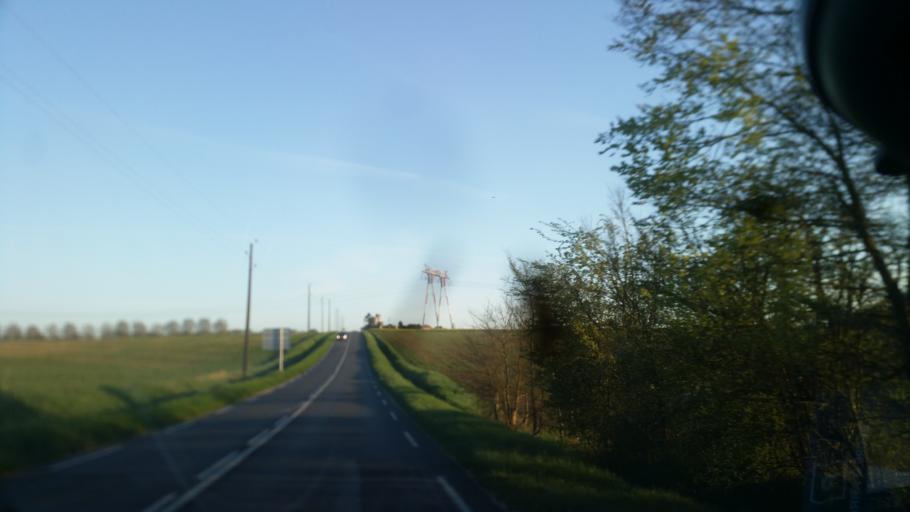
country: FR
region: Ile-de-France
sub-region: Departement de l'Essonne
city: Limours
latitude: 48.6309
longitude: 2.0661
